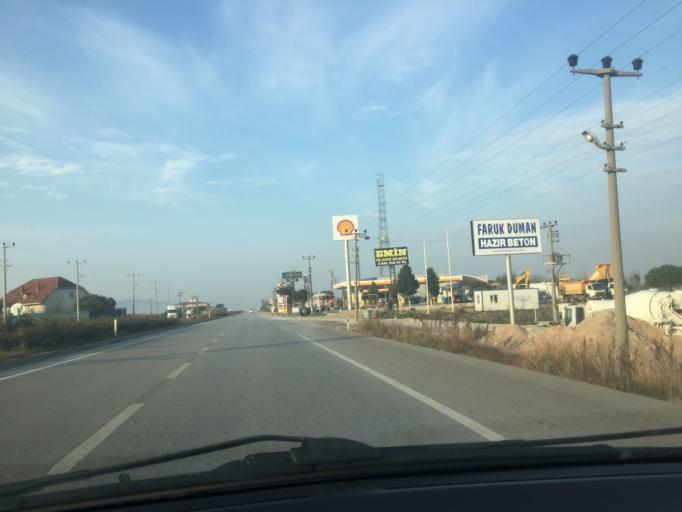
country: TR
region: Canakkale
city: Dimetoka
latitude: 40.2466
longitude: 27.2847
